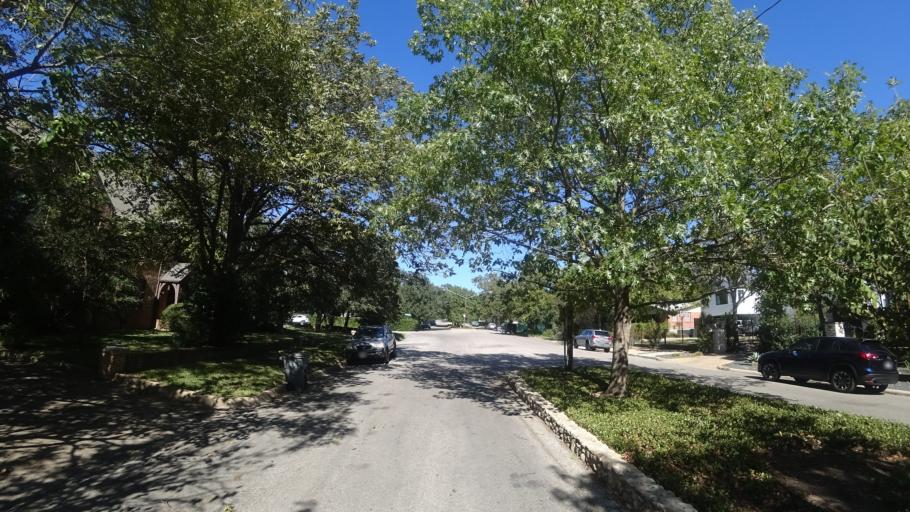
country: US
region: Texas
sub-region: Travis County
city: Austin
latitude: 30.2843
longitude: -97.7599
